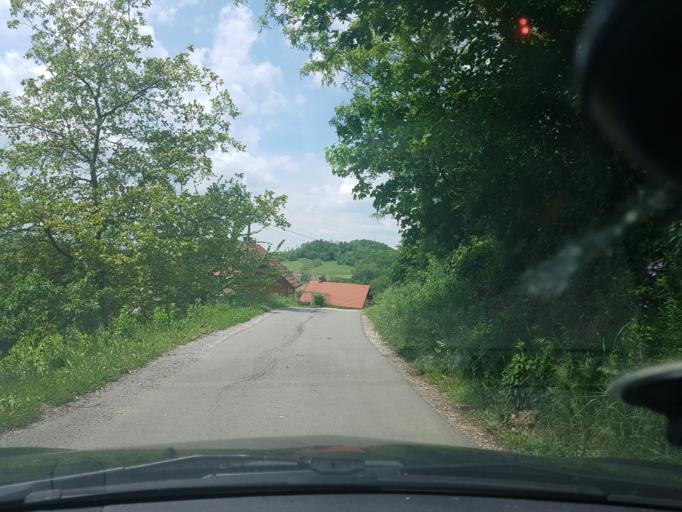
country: SI
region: Rogatec
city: Rogatec
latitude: 46.2151
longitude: 15.7137
